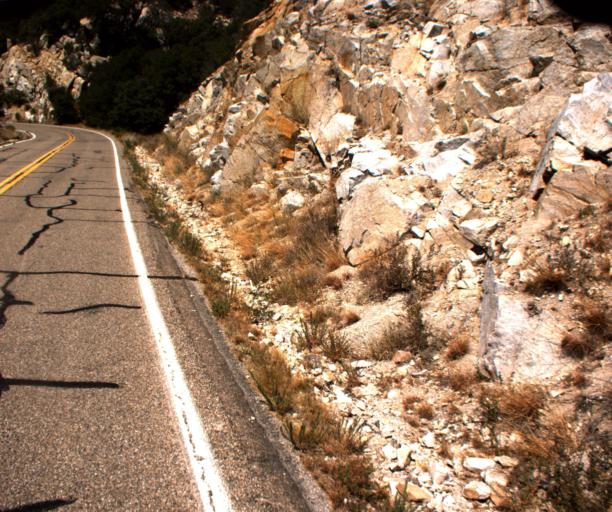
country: US
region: Arizona
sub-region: Pima County
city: Sells
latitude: 31.9485
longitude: -111.6187
